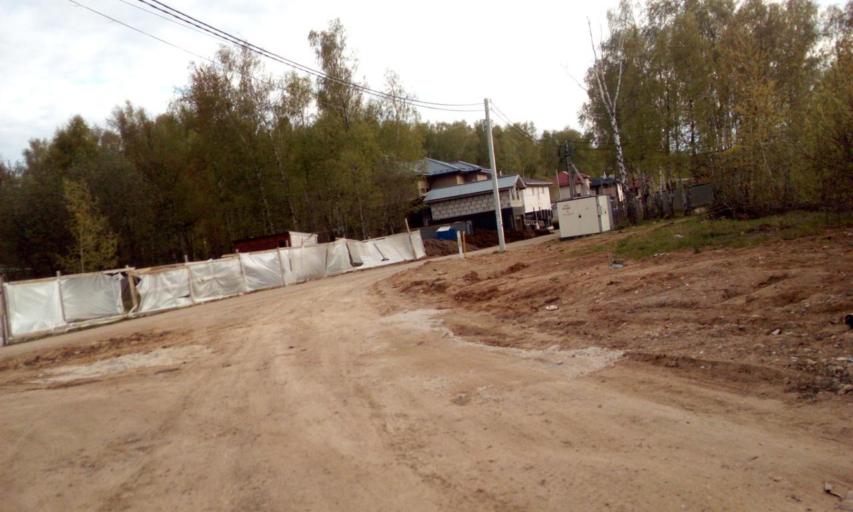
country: RU
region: Moskovskaya
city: Kokoshkino
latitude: 55.6452
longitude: 37.1557
